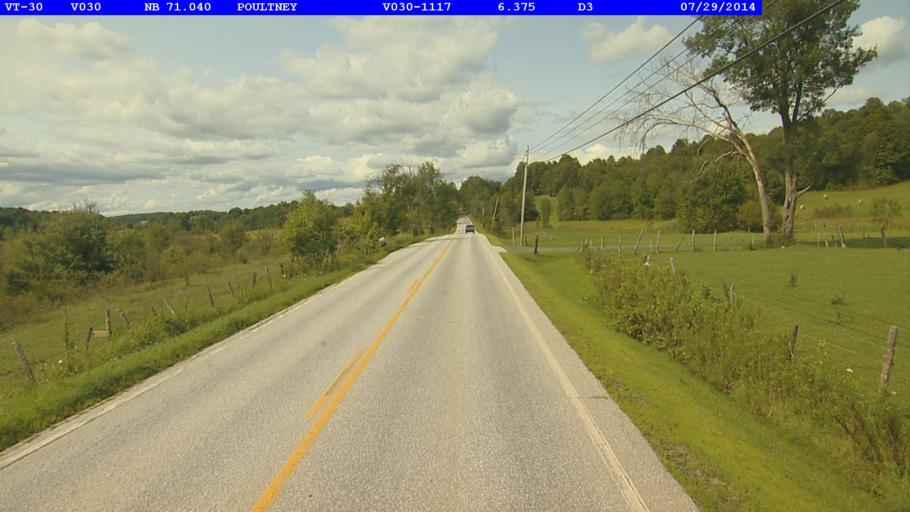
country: US
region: Vermont
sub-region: Rutland County
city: Poultney
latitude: 43.5428
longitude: -73.2276
